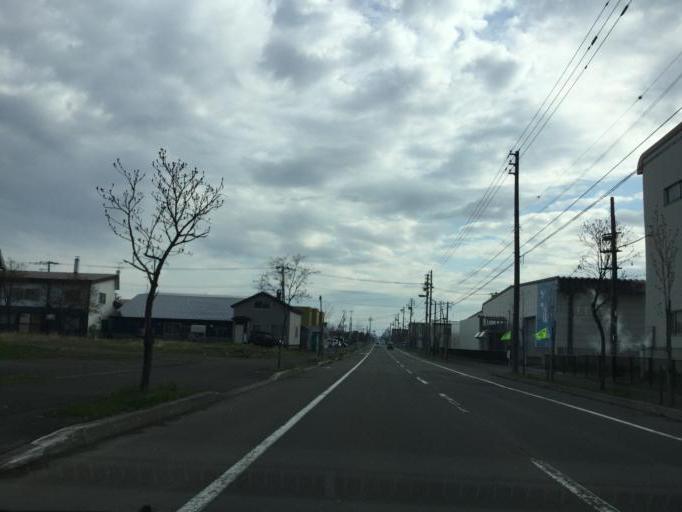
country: JP
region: Hokkaido
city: Iwamizawa
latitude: 43.1883
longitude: 141.7449
